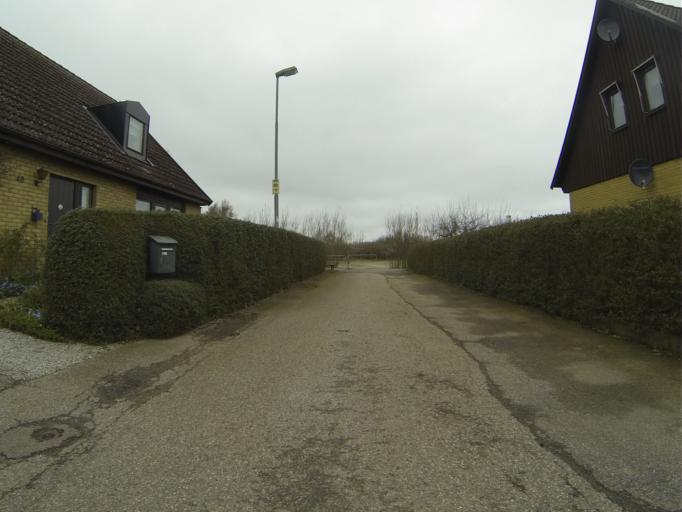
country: SE
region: Skane
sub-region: Simrishamns Kommun
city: Simrishamn
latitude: 55.5423
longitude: 14.3448
